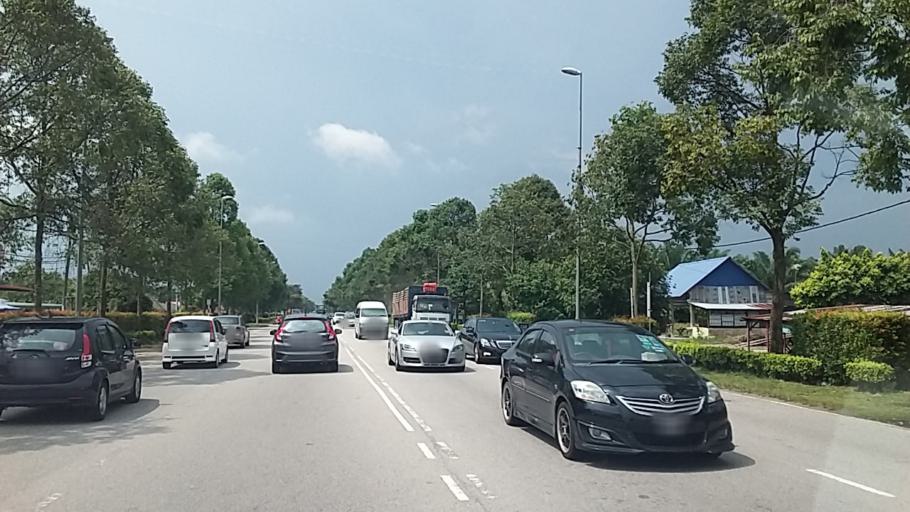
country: MY
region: Johor
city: Parit Raja
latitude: 1.8585
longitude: 103.1012
